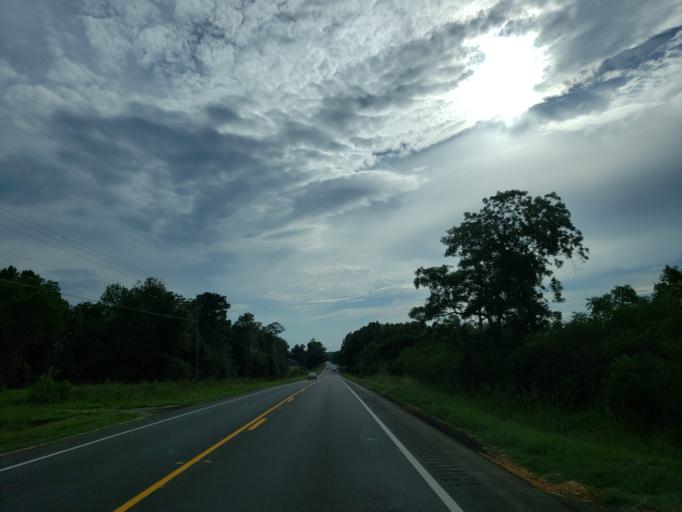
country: US
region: Georgia
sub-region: Irwin County
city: Ocilla
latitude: 31.5631
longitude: -83.3484
